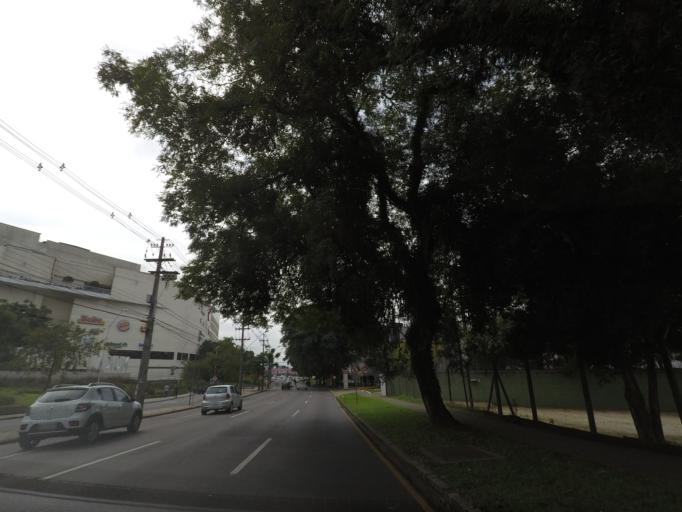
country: BR
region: Parana
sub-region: Curitiba
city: Curitiba
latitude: -25.4787
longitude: -49.2899
